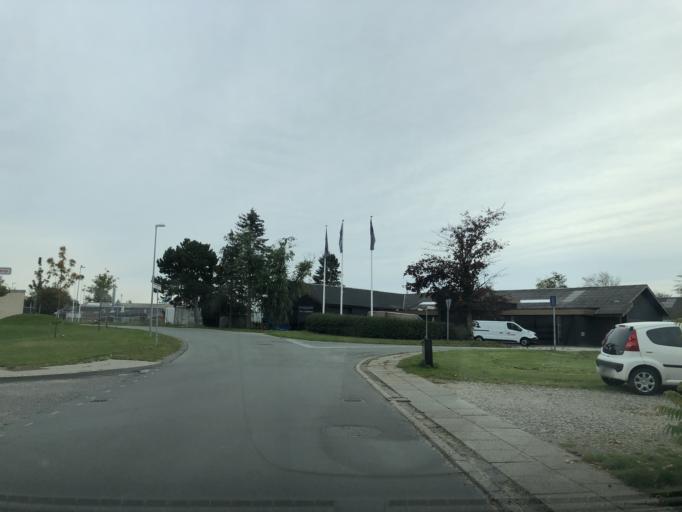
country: DK
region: Central Jutland
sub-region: Syddjurs Kommune
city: Hornslet
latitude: 56.3085
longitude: 10.3097
